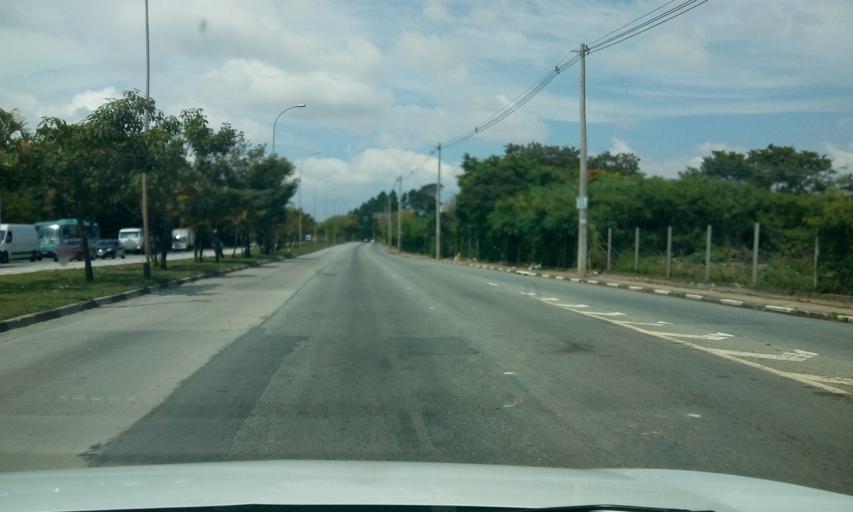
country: BR
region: Sao Paulo
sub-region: Guarulhos
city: Guarulhos
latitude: -23.4488
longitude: -46.4943
